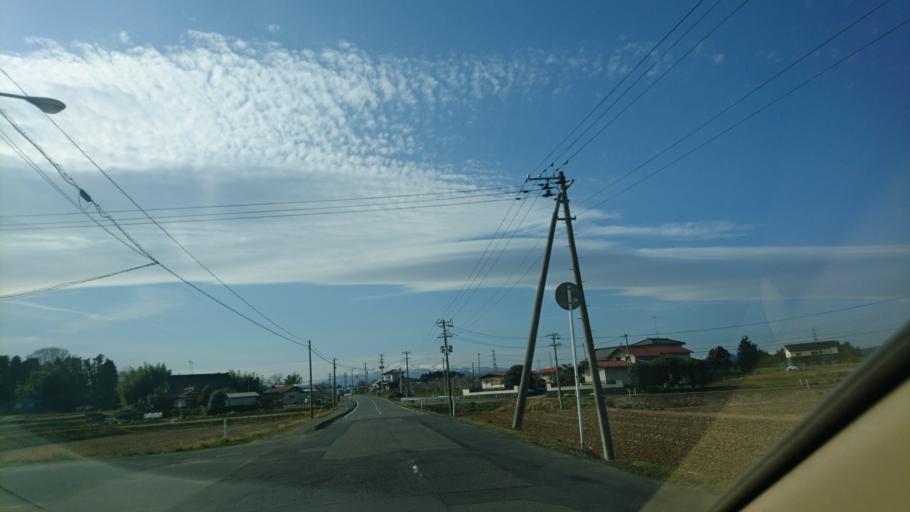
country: JP
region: Iwate
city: Ichinoseki
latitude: 38.8057
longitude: 141.0397
